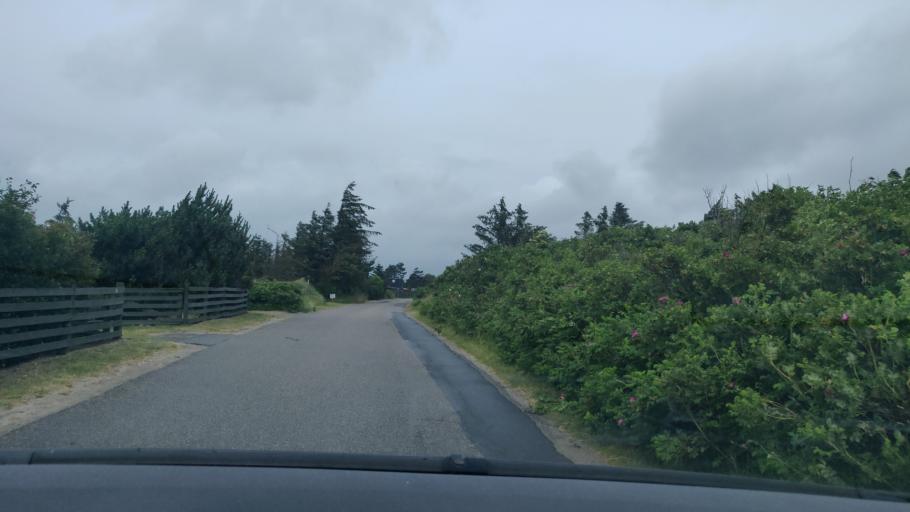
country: DK
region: North Denmark
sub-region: Jammerbugt Kommune
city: Pandrup
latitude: 57.2551
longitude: 9.5944
